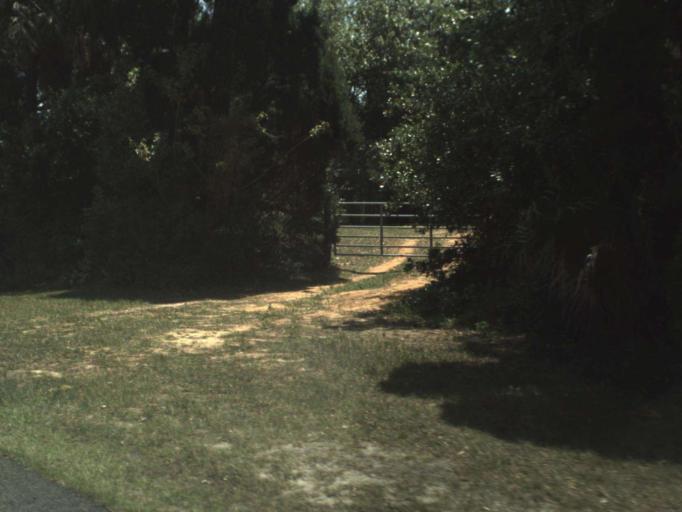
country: US
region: Florida
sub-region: Volusia County
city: Ponce Inlet
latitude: 29.0790
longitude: -80.9550
